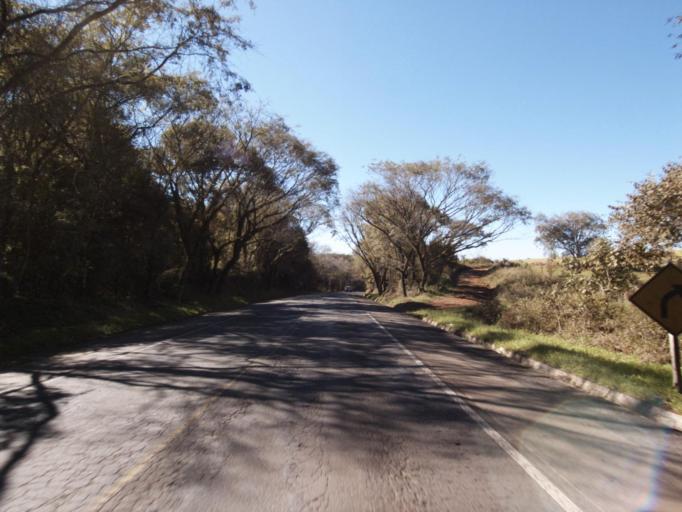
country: BR
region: Santa Catarina
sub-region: Sao Lourenco Do Oeste
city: Sao Lourenco dOeste
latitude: -26.8288
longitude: -53.1170
